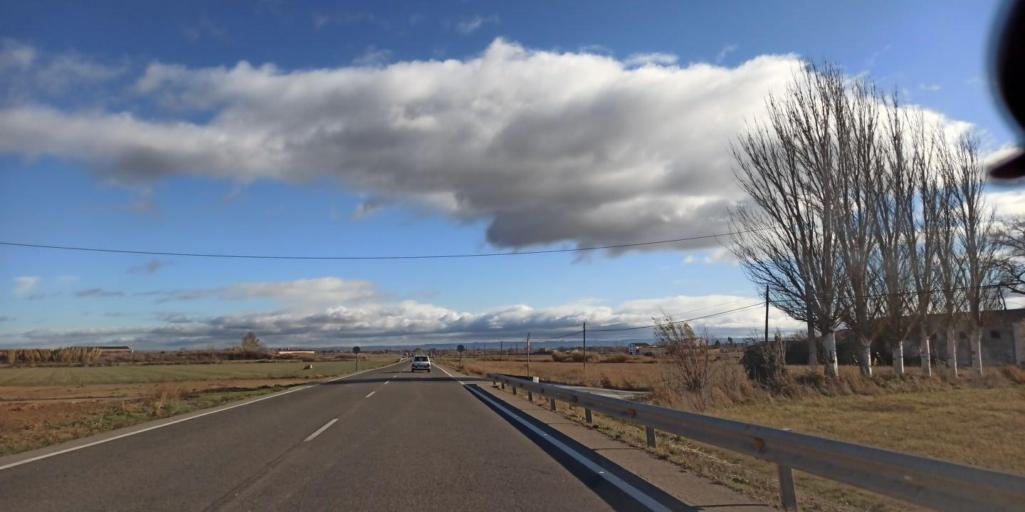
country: ES
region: Catalonia
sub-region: Provincia de Lleida
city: Penelles
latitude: 41.7441
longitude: 0.9426
